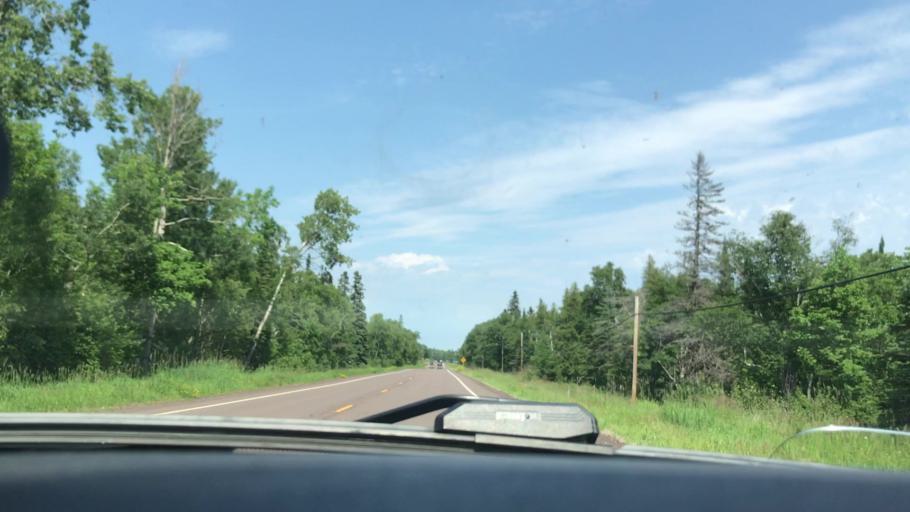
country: US
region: Minnesota
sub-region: Cook County
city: Grand Marais
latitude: 47.6340
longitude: -90.7187
